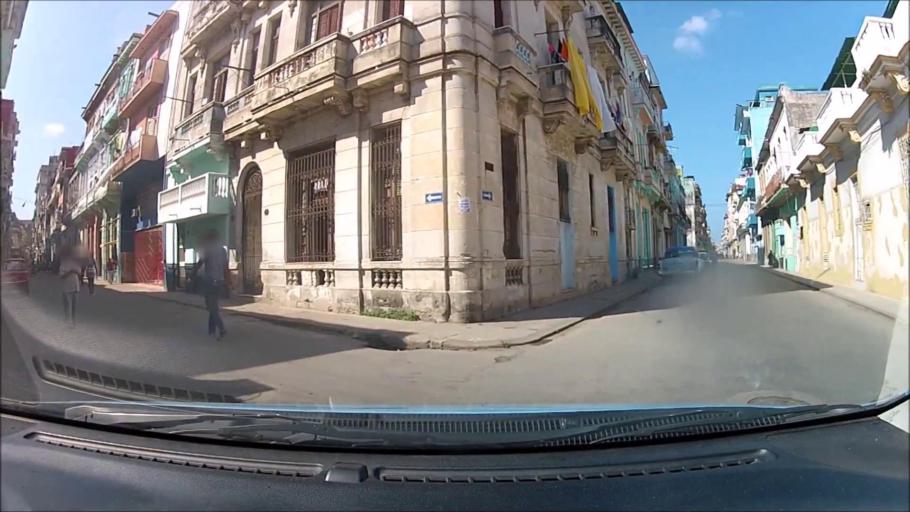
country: CU
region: La Habana
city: Centro Habana
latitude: 23.1392
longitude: -82.3659
